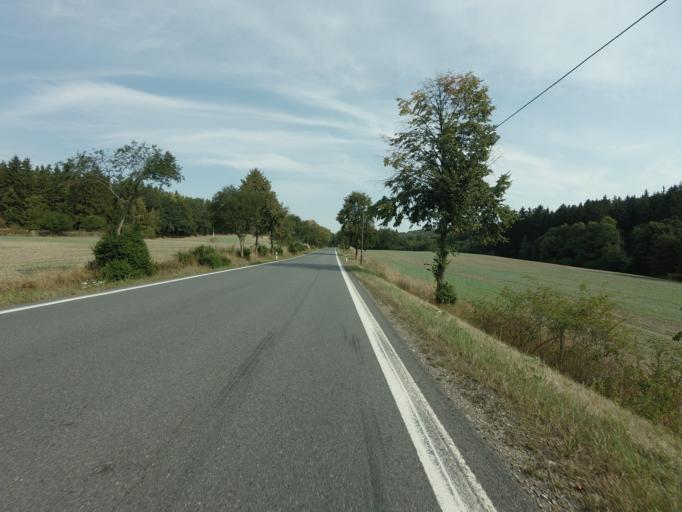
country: CZ
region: Central Bohemia
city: Petrovice
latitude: 49.5263
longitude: 14.3546
